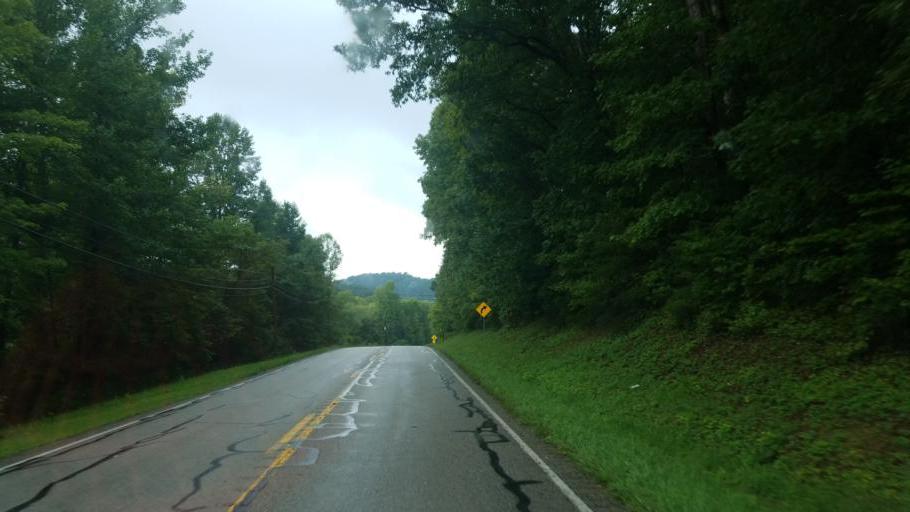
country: US
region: Kentucky
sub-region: Rowan County
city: Morehead
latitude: 38.1520
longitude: -83.4750
